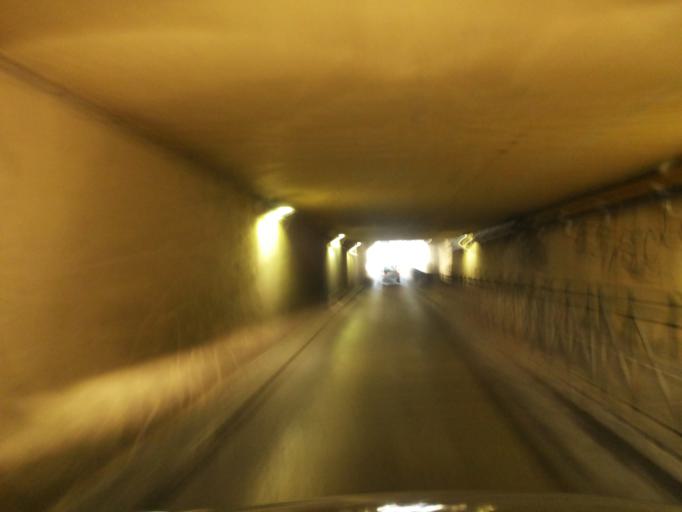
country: IT
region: Piedmont
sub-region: Provincia di Vercelli
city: Vercelli
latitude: 45.3315
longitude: 8.4202
